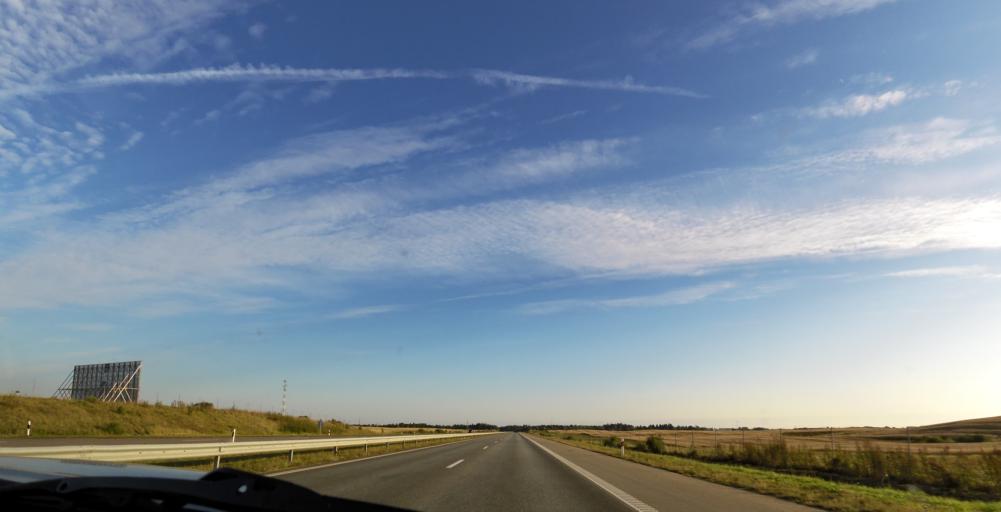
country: LT
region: Vilnius County
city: Ukmerge
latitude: 55.1950
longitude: 24.8130
